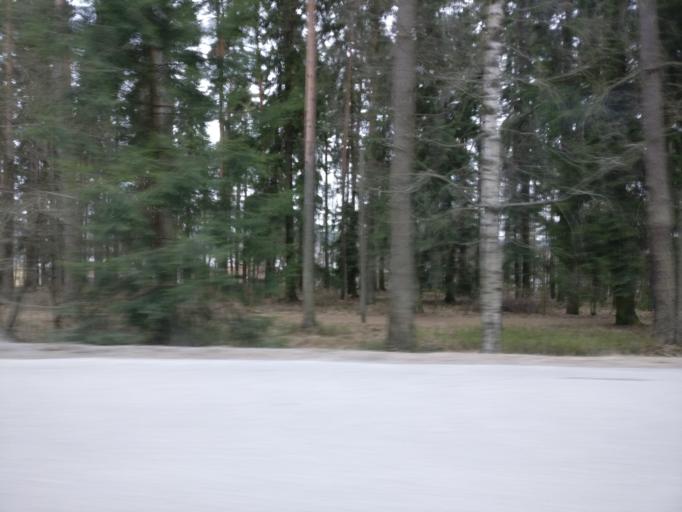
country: FI
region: Pirkanmaa
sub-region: Tampere
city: Tampere
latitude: 61.4904
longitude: 23.8137
